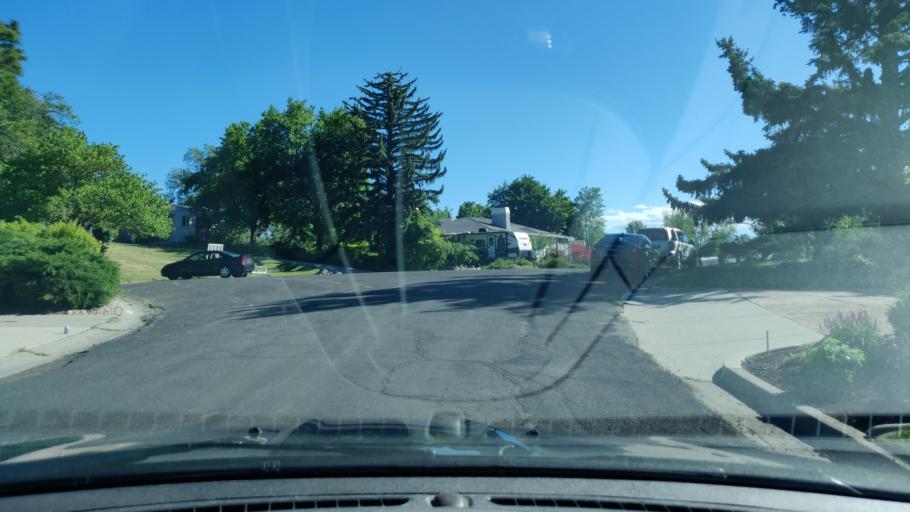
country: US
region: Utah
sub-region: Salt Lake County
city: Cottonwood Heights
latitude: 40.6119
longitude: -111.8113
